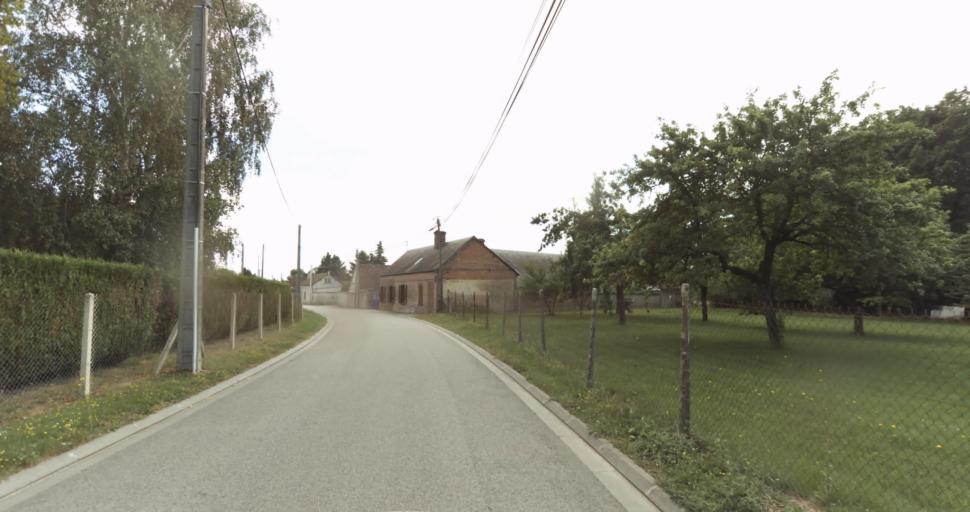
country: FR
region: Haute-Normandie
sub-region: Departement de l'Eure
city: Nonancourt
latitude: 48.8371
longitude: 1.1655
